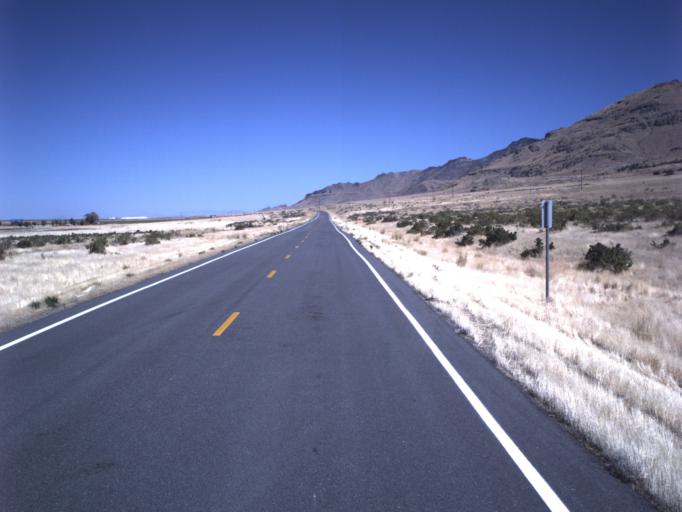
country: US
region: Utah
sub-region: Tooele County
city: Grantsville
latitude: 40.6628
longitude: -112.6778
